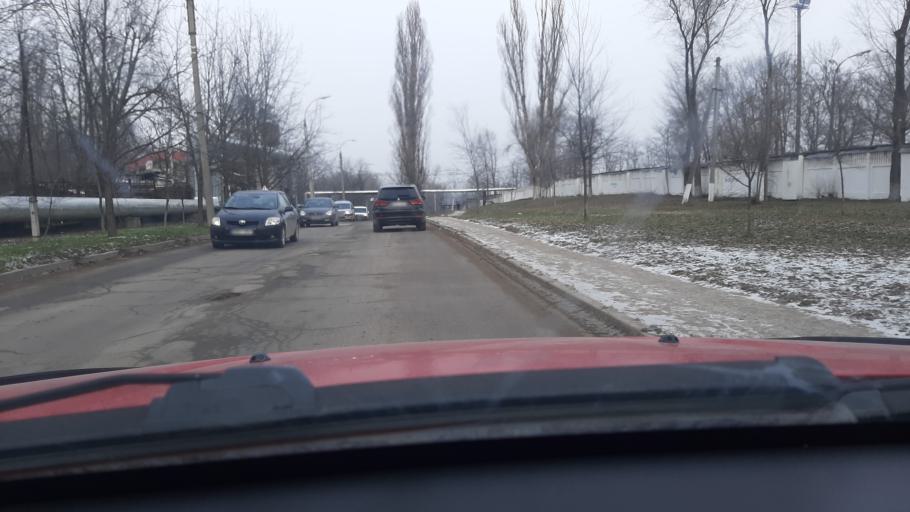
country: MD
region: Chisinau
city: Chisinau
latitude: 46.9767
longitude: 28.8928
